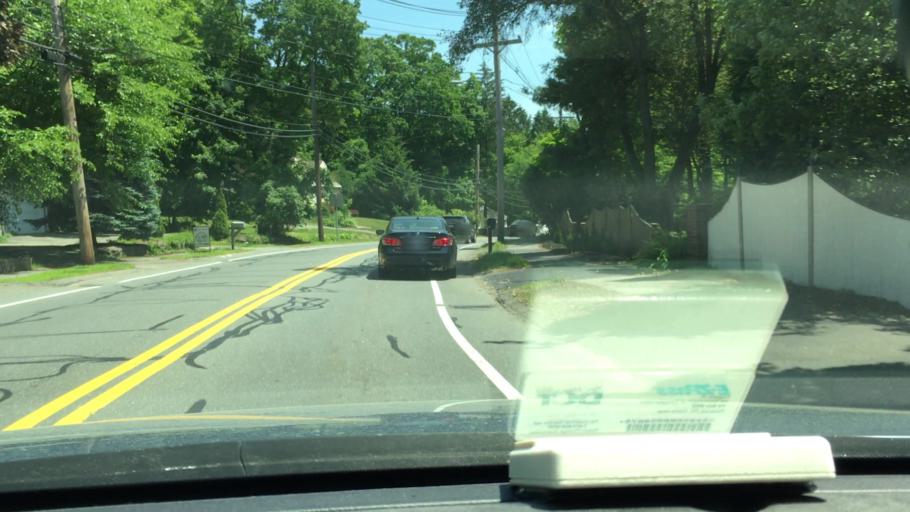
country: US
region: Massachusetts
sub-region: Middlesex County
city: Lexington
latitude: 42.4440
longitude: -71.1956
